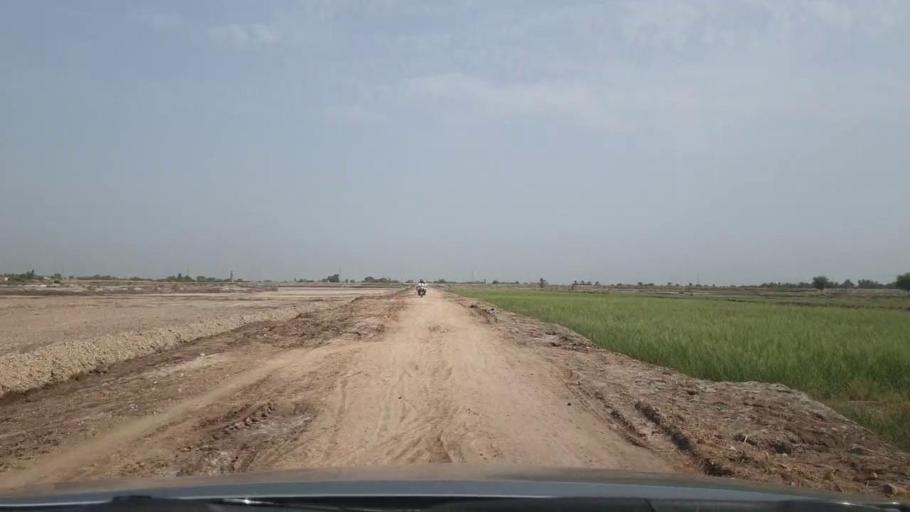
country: PK
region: Sindh
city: Rohri
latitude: 27.6749
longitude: 69.0261
